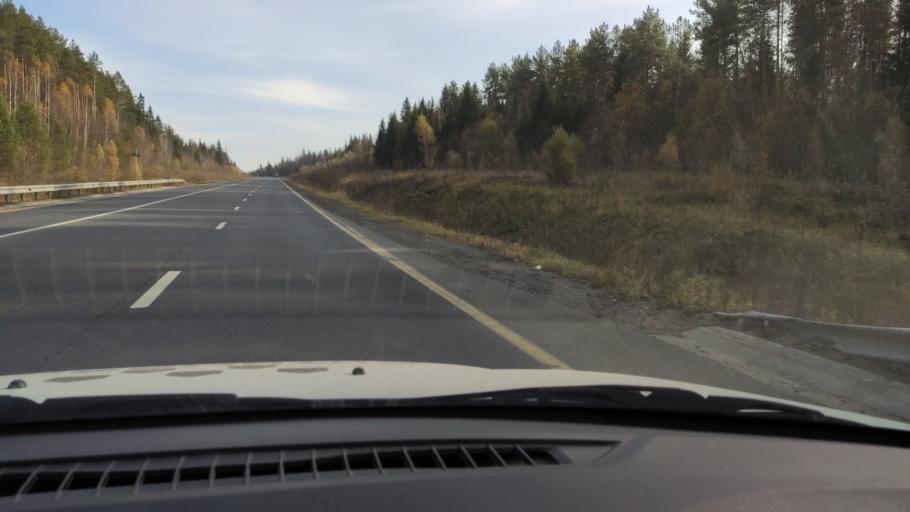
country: RU
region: Perm
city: Novyye Lyady
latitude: 58.0356
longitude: 56.4735
